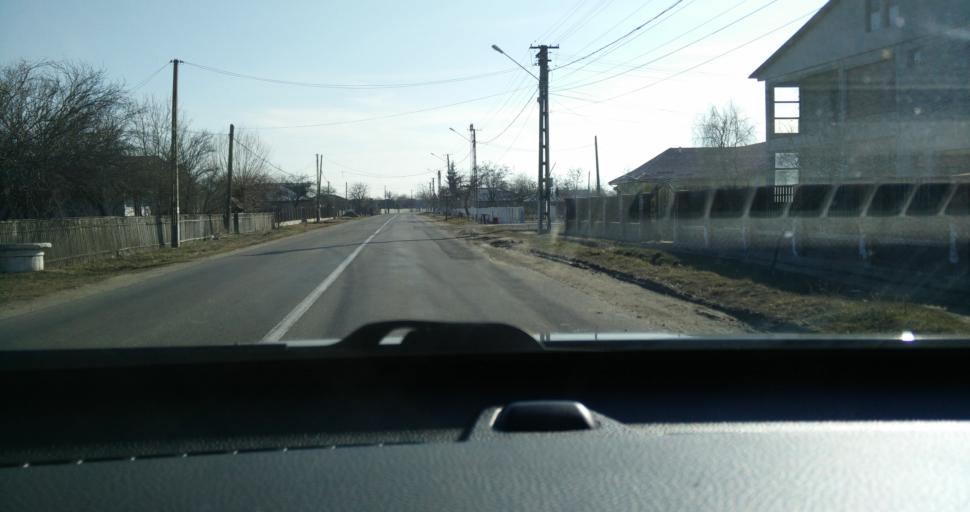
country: RO
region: Vrancea
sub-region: Comuna Nanesti
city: Nanesti
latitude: 45.5462
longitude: 27.4991
